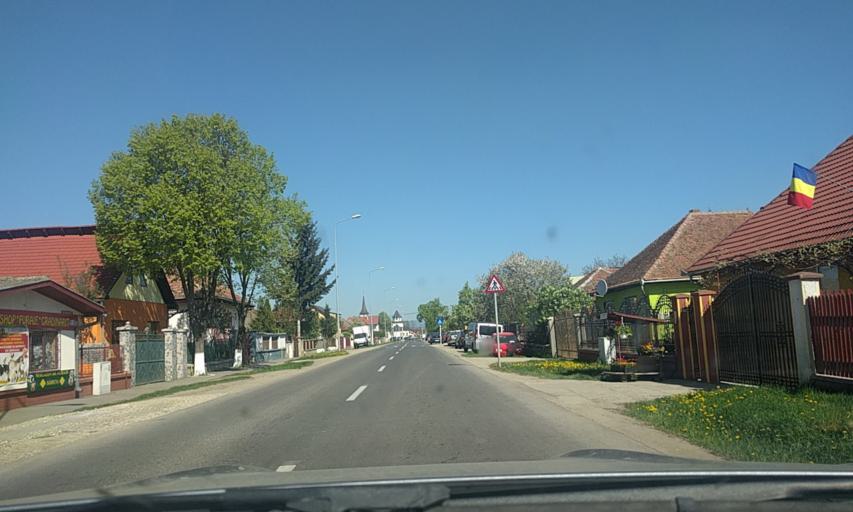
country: RO
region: Brasov
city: Brasov
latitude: 45.6958
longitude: 25.5604
